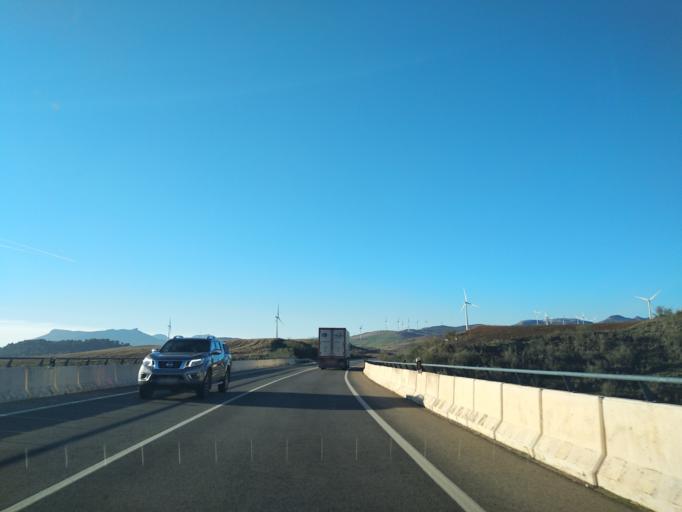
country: ES
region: Andalusia
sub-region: Provincia de Malaga
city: Teba
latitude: 36.9554
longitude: -4.8588
